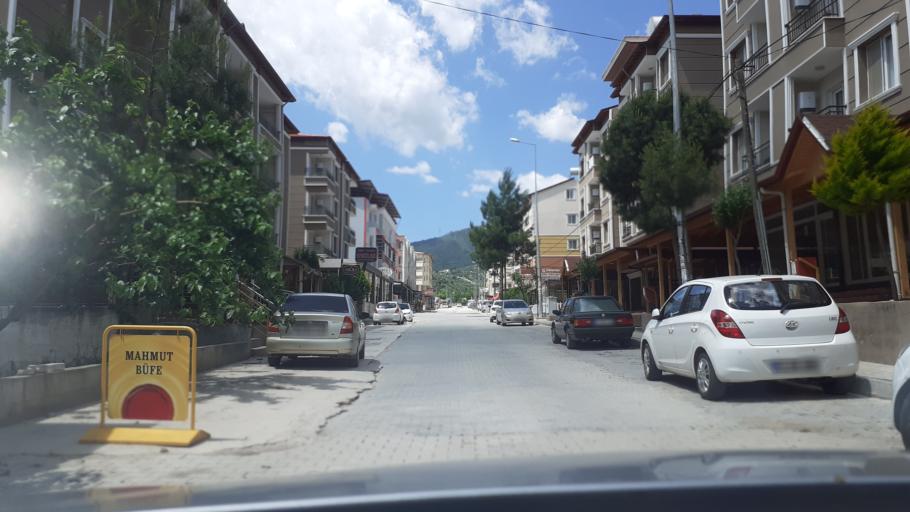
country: TR
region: Hatay
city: Anayazi
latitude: 36.3339
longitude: 36.2026
